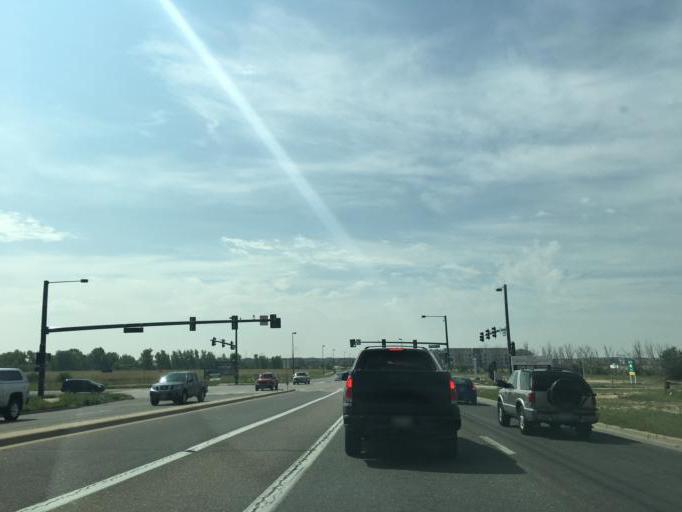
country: US
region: Colorado
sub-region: Adams County
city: Aurora
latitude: 39.7991
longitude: -104.7722
